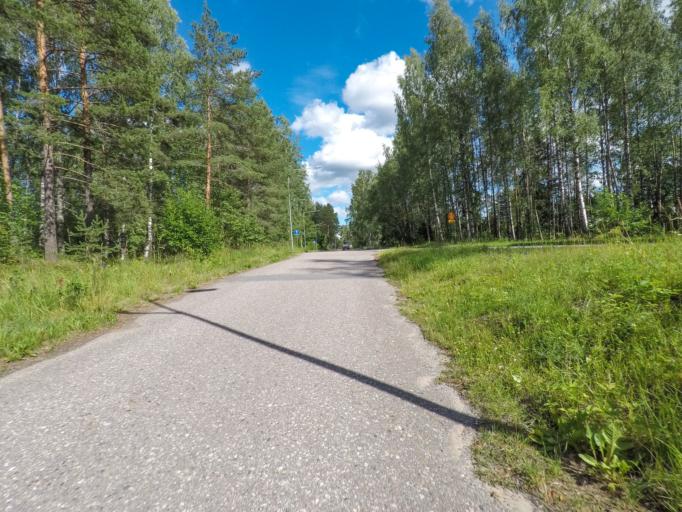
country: FI
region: South Karelia
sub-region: Lappeenranta
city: Lappeenranta
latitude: 61.0788
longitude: 28.3132
